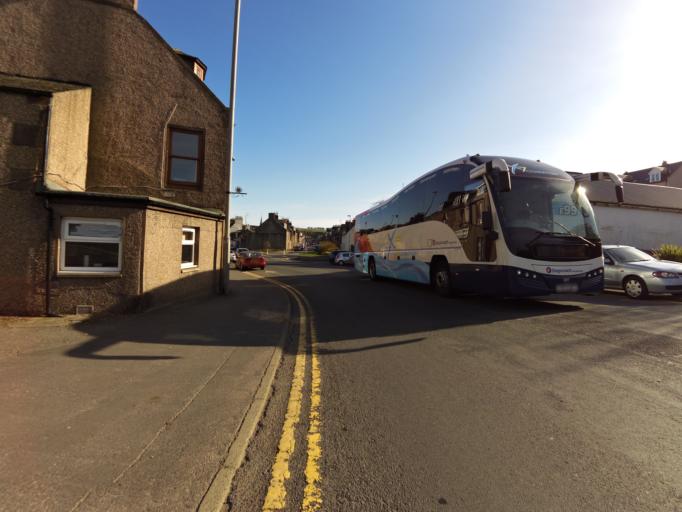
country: GB
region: Scotland
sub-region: Aberdeenshire
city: Stonehaven
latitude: 56.9675
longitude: -2.2095
